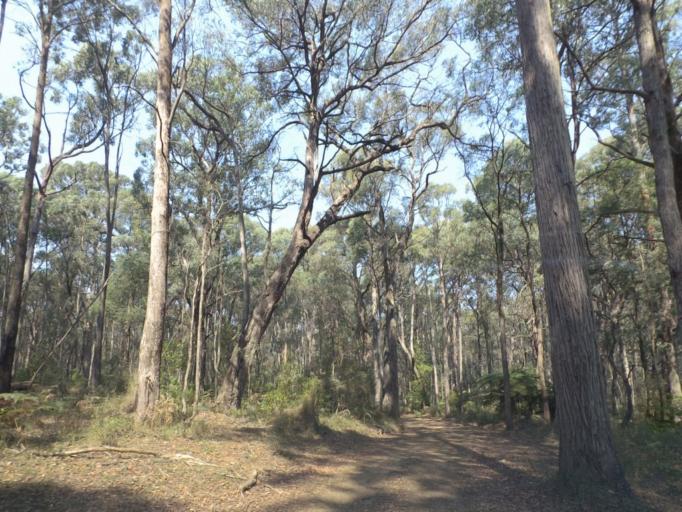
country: AU
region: Victoria
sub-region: Yarra Ranges
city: Healesville
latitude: -37.5784
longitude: 145.6633
